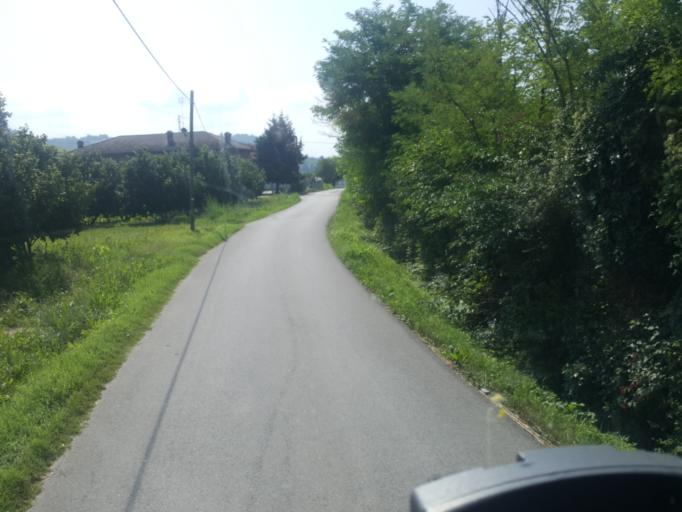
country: IT
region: Piedmont
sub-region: Provincia di Cuneo
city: Narzole
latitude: 44.5974
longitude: 7.8932
